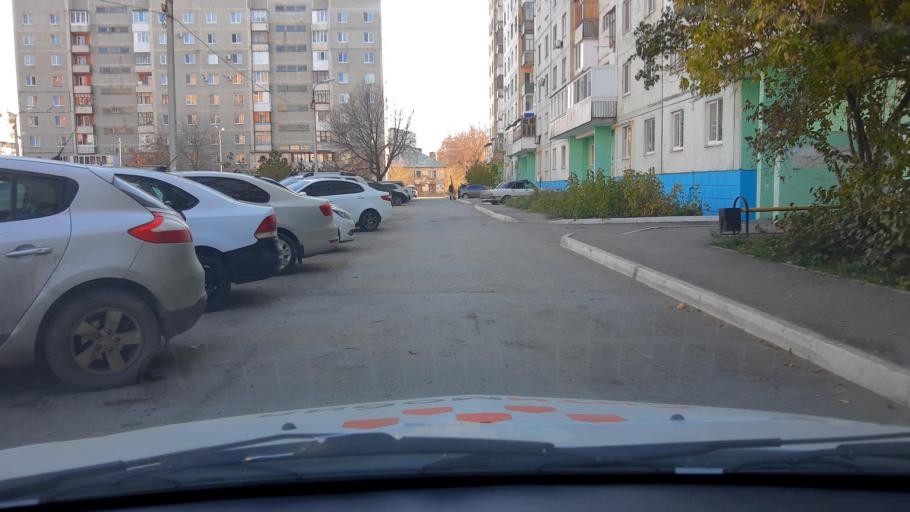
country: RU
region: Bashkortostan
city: Mikhaylovka
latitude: 54.7865
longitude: 55.8861
